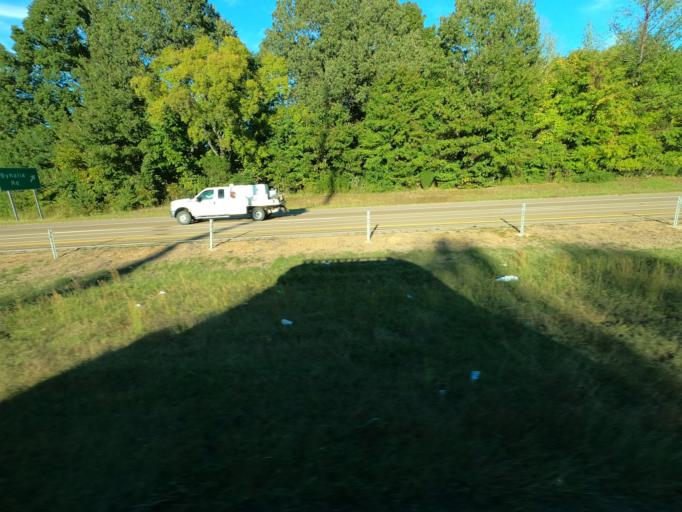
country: US
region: Tennessee
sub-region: Shelby County
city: Collierville
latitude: 35.0289
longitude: -89.6827
